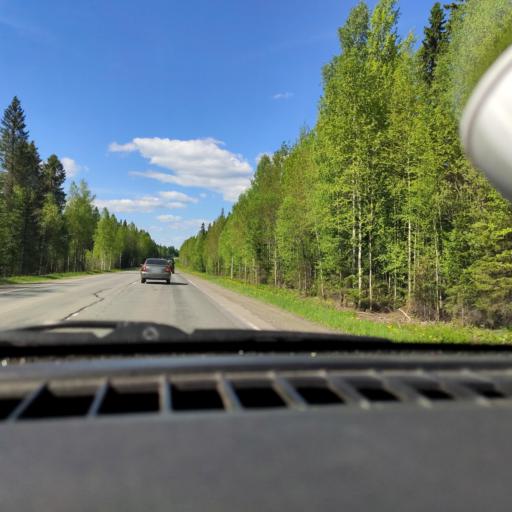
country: RU
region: Perm
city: Perm
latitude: 58.2326
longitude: 56.1613
